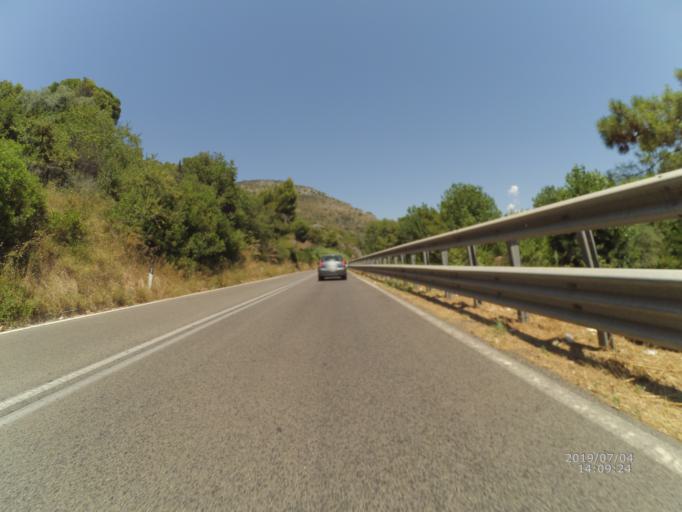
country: IT
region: Latium
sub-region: Provincia di Latina
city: Terracina
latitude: 41.2957
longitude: 13.2668
